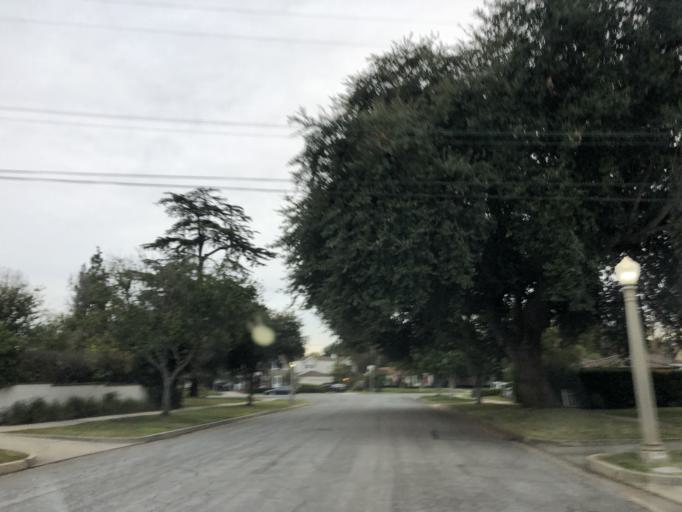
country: US
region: California
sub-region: Los Angeles County
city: San Marino
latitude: 34.1172
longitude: -118.1032
